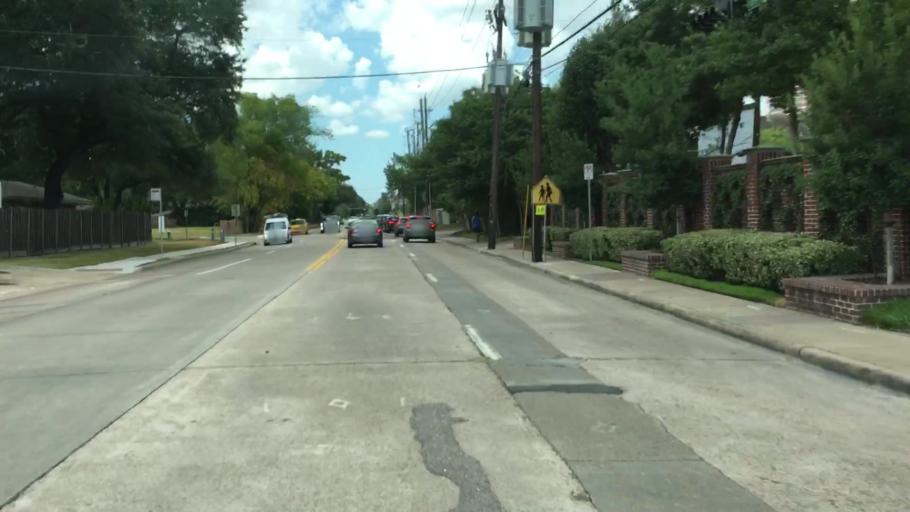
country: US
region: Texas
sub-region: Harris County
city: Hunters Creek Village
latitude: 29.7462
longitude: -95.4670
